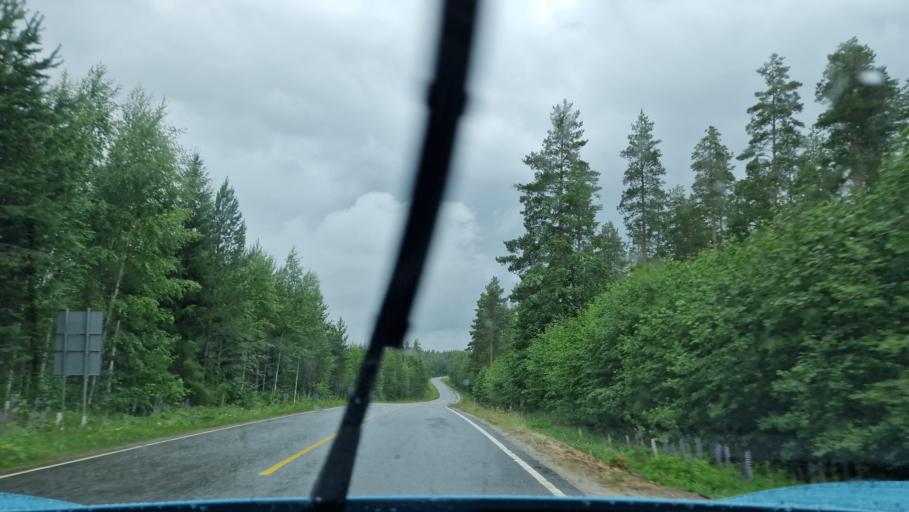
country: FI
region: Southern Ostrobothnia
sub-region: Jaerviseutu
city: Soini
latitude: 62.7887
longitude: 24.3841
